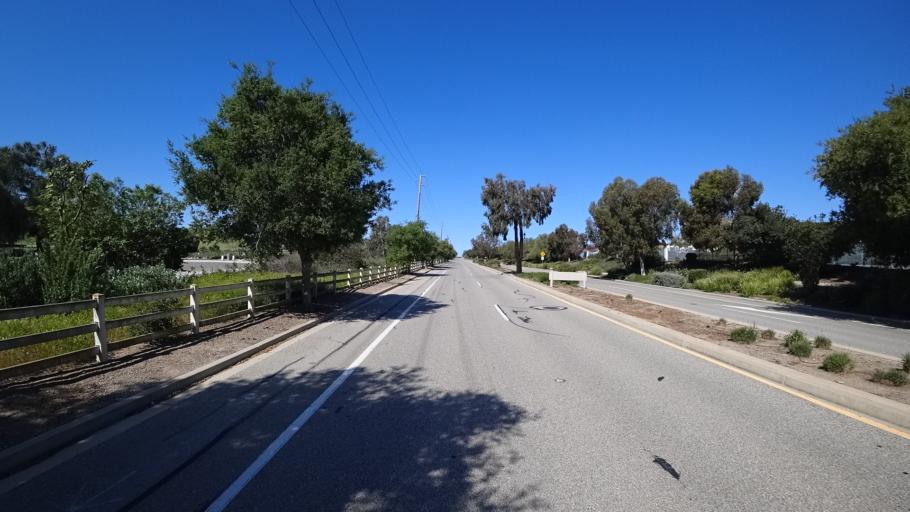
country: US
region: California
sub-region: Ventura County
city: Casa Conejo
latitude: 34.1563
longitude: -118.9785
